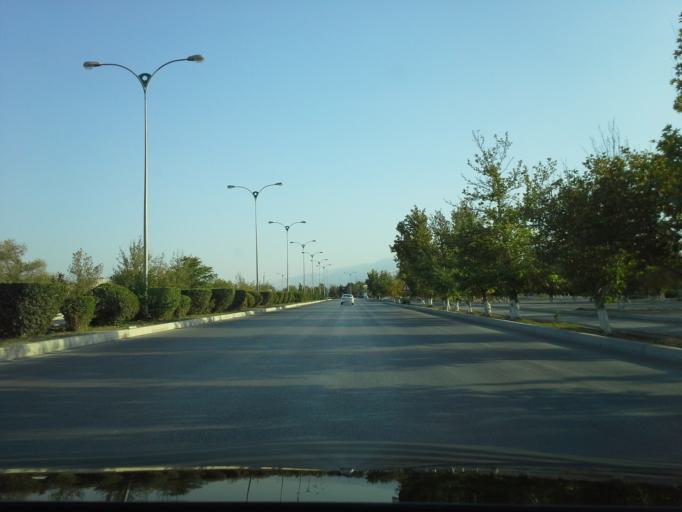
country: TM
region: Ahal
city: Abadan
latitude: 38.0377
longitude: 58.1875
